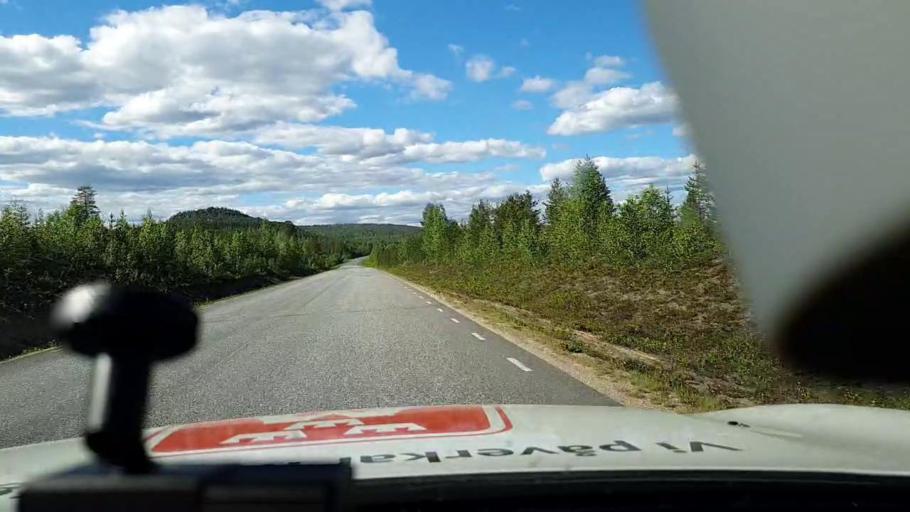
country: FI
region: Lapland
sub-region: Torniolaakso
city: Ylitornio
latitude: 66.2990
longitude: 23.6343
